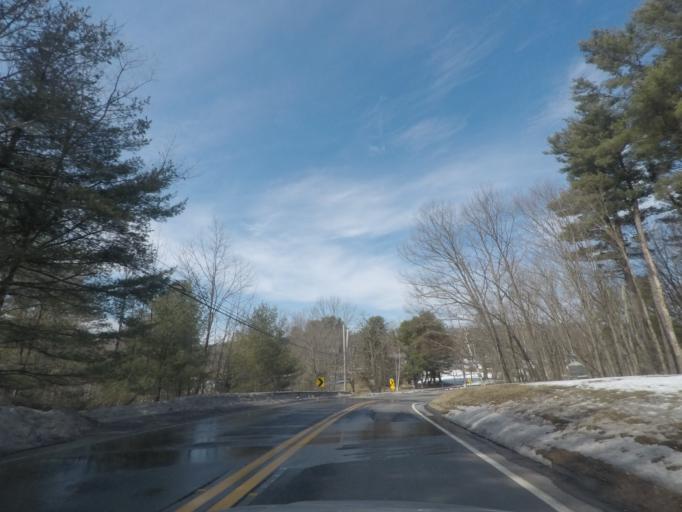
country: US
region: Massachusetts
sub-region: Berkshire County
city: West Stockbridge
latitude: 42.3511
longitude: -73.3849
